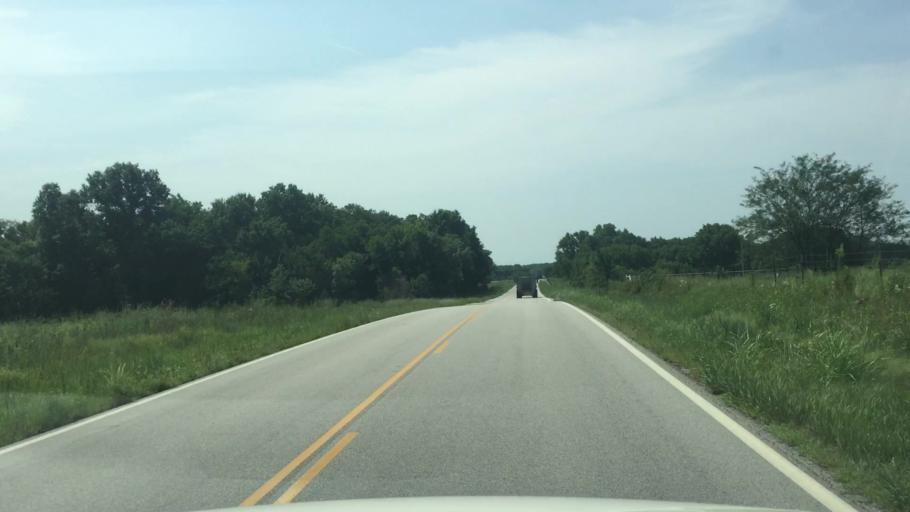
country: US
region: Kansas
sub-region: Montgomery County
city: Cherryvale
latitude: 37.2042
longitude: -95.5577
